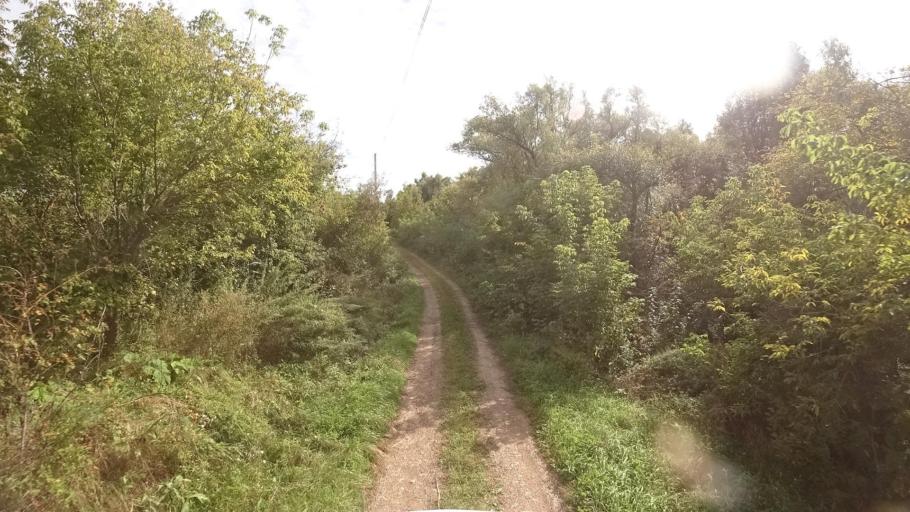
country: RU
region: Primorskiy
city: Dostoyevka
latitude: 44.3265
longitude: 133.4847
